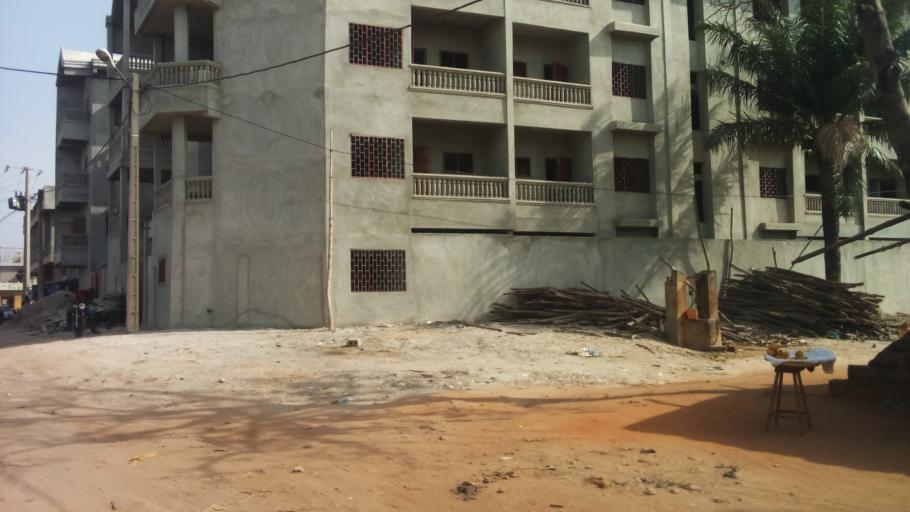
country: BJ
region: Atlantique
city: Abomey-Calavi
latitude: 6.4283
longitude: 2.3282
